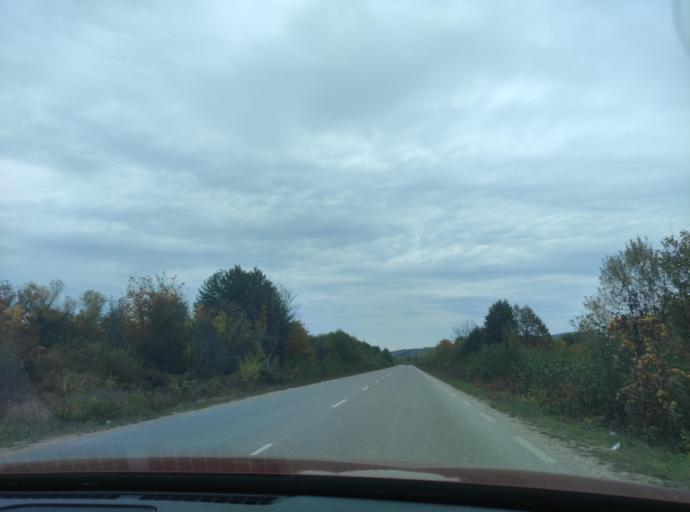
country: BG
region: Montana
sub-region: Obshtina Berkovitsa
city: Berkovitsa
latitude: 43.2367
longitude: 23.1605
